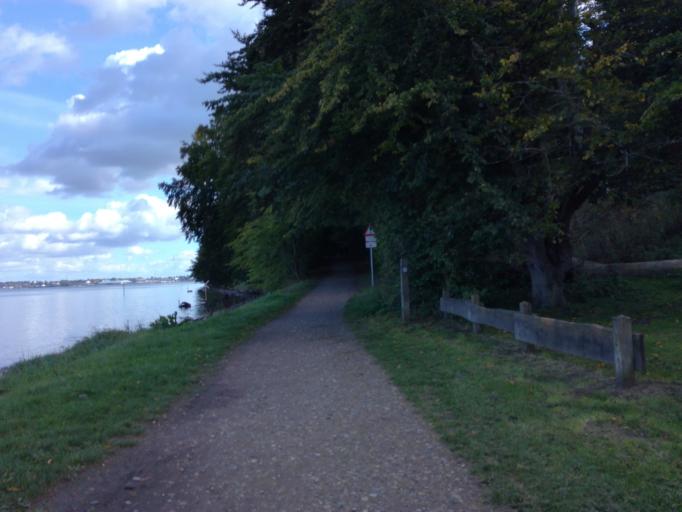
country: DK
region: South Denmark
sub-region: Fredericia Kommune
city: Snoghoj
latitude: 55.5116
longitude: 9.7117
